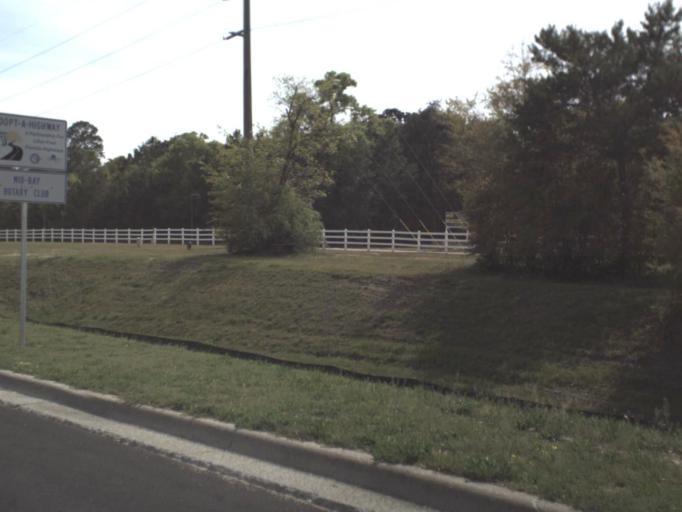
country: US
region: Florida
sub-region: Okaloosa County
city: Niceville
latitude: 30.5030
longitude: -86.4392
